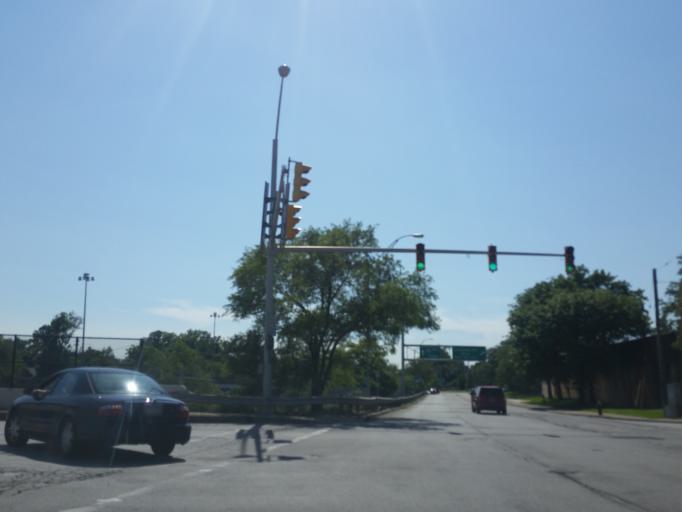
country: US
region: Ohio
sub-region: Cuyahoga County
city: Lakewood
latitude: 41.4700
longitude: -81.7971
